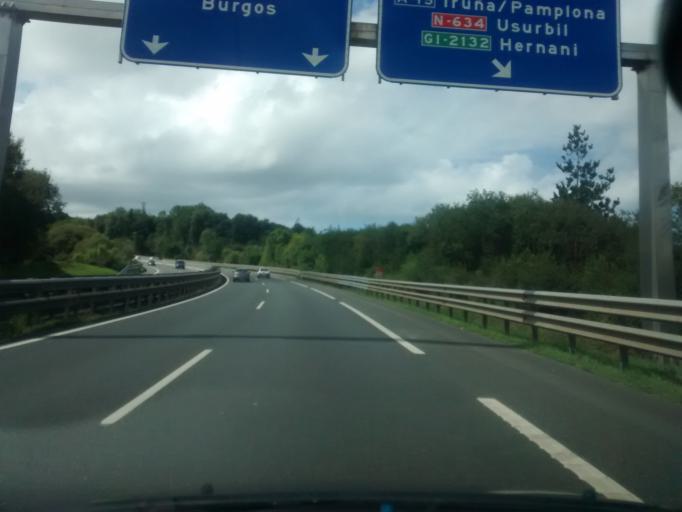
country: ES
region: Basque Country
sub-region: Provincia de Guipuzcoa
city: San Sebastian
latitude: 43.2989
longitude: -2.0039
